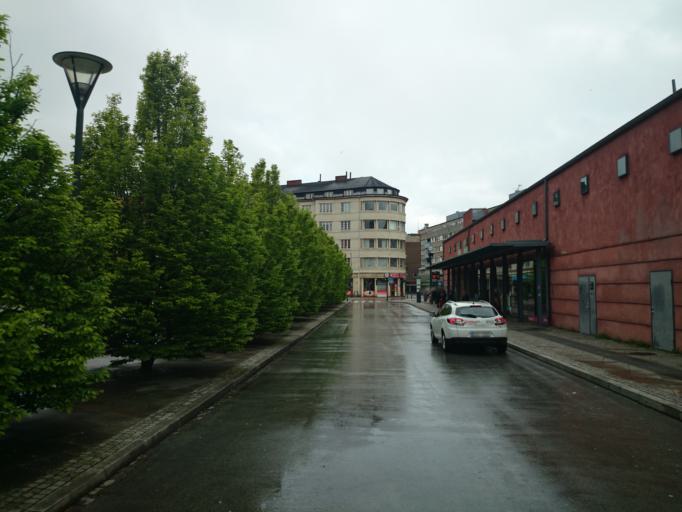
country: SE
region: Skane
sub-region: Malmo
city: Malmoe
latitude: 55.6054
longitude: 13.0235
